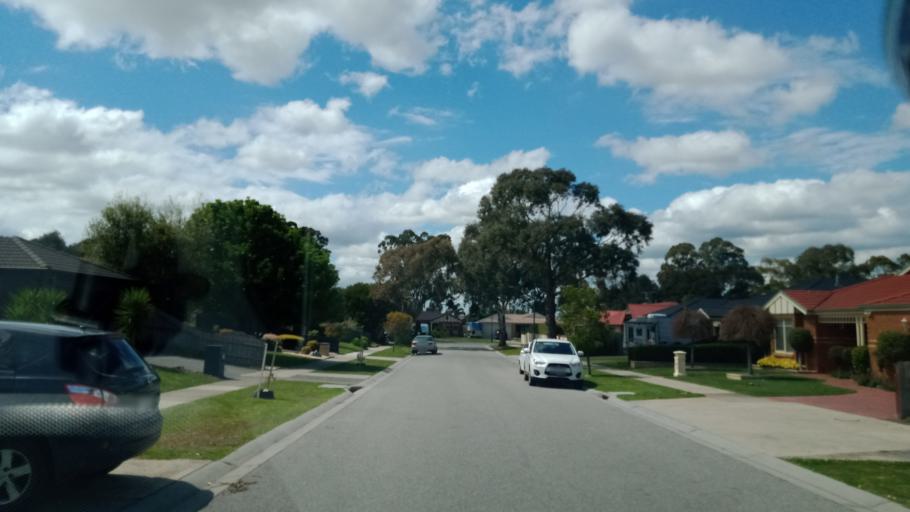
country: AU
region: Victoria
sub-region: Frankston
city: Sandhurst
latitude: -38.0961
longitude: 145.1965
